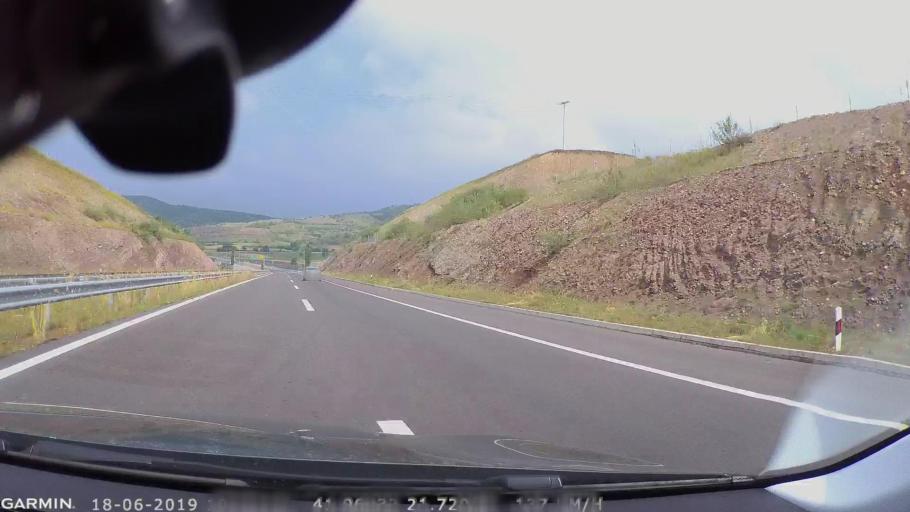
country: MK
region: Sveti Nikole
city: Gorobinci
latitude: 41.9336
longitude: 21.8256
